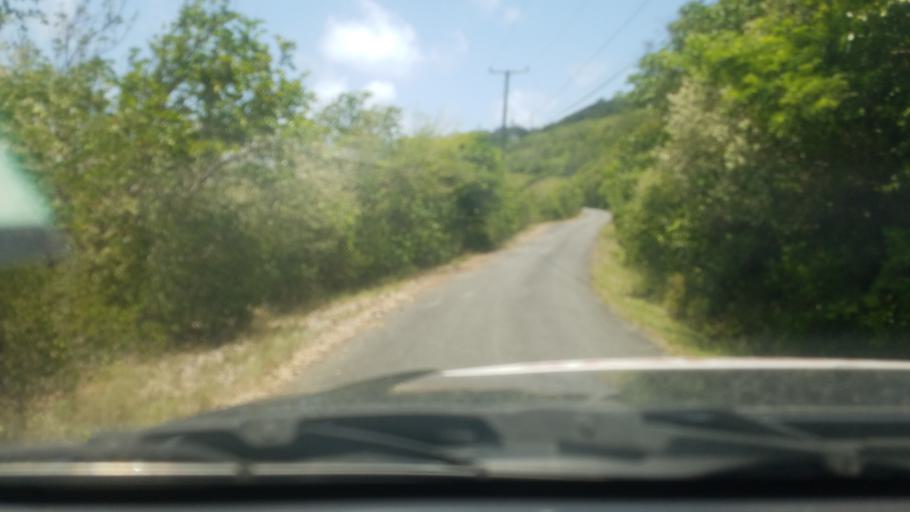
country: LC
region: Vieux-Fort
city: Vieux Fort
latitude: 13.7139
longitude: -60.9473
